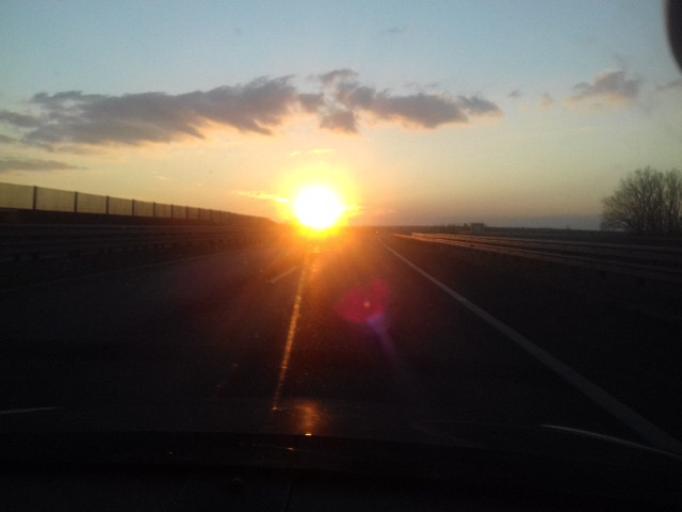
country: HU
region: Hajdu-Bihar
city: Gorbehaza
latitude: 47.7945
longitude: 21.2713
